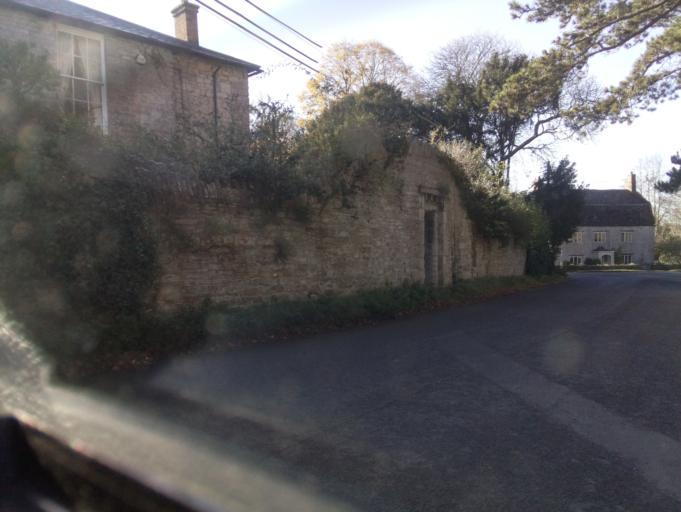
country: GB
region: England
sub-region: Somerset
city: Langport
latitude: 51.0359
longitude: -2.8187
